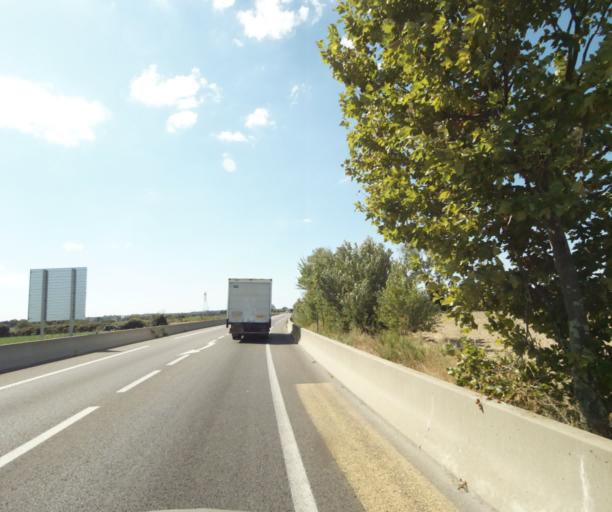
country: FR
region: Languedoc-Roussillon
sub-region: Departement du Gard
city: Rodilhan
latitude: 43.8229
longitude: 4.4191
